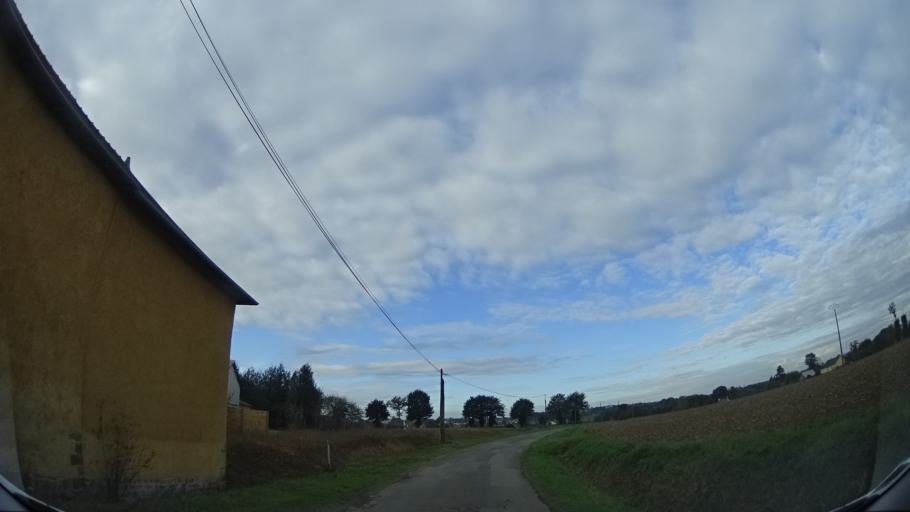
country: FR
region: Brittany
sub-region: Departement d'Ille-et-Vilaine
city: Geveze
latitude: 48.2264
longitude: -1.7825
